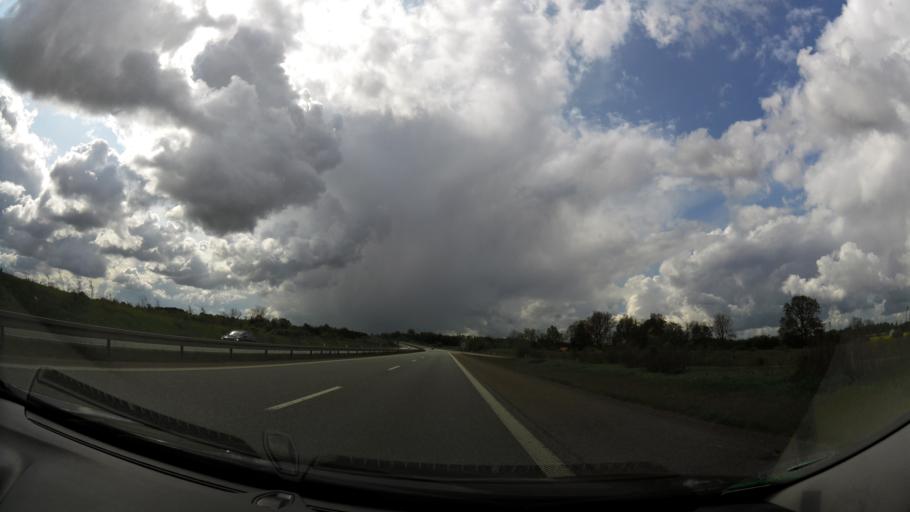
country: DK
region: South Denmark
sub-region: Faaborg-Midtfyn Kommune
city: Ringe
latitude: 55.2183
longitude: 10.5017
